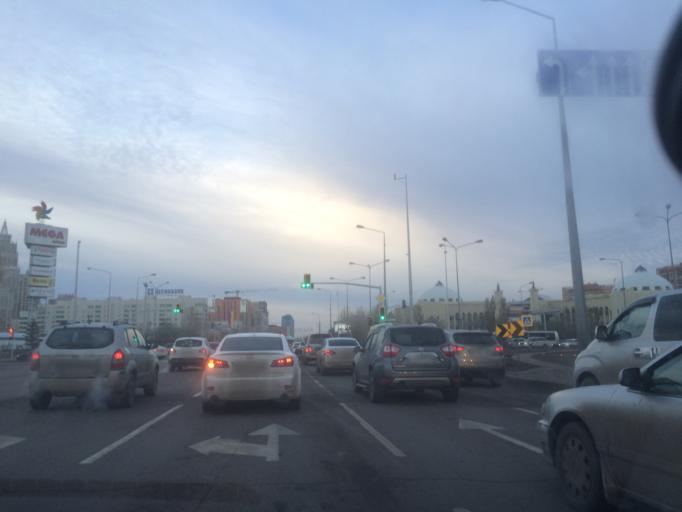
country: KZ
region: Astana Qalasy
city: Astana
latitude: 51.1467
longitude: 71.4121
